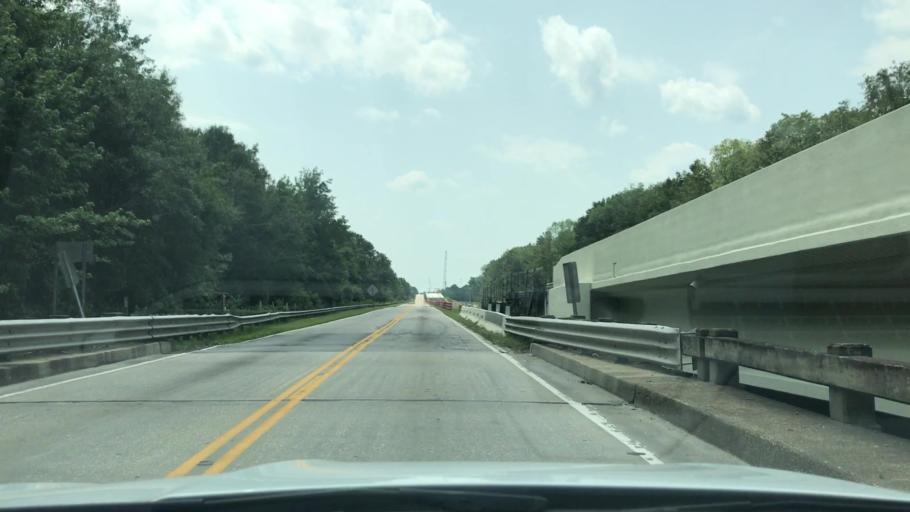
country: US
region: South Carolina
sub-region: Horry County
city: Socastee
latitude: 33.6667
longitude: -79.1457
